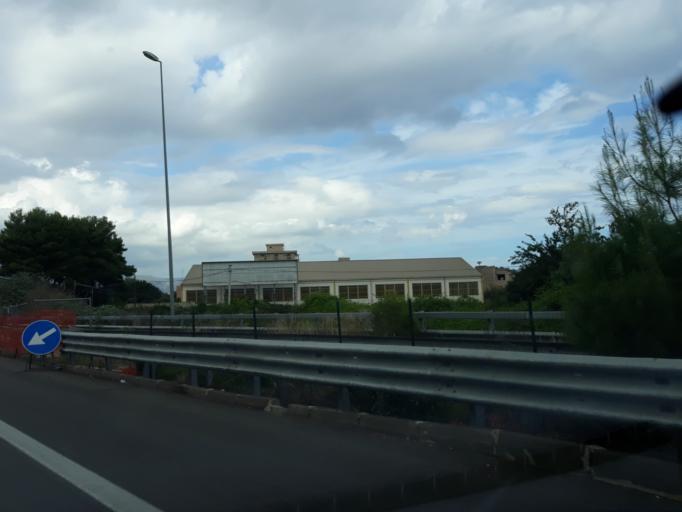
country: IT
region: Sicily
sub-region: Palermo
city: Ciaculli
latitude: 38.0873
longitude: 13.3992
